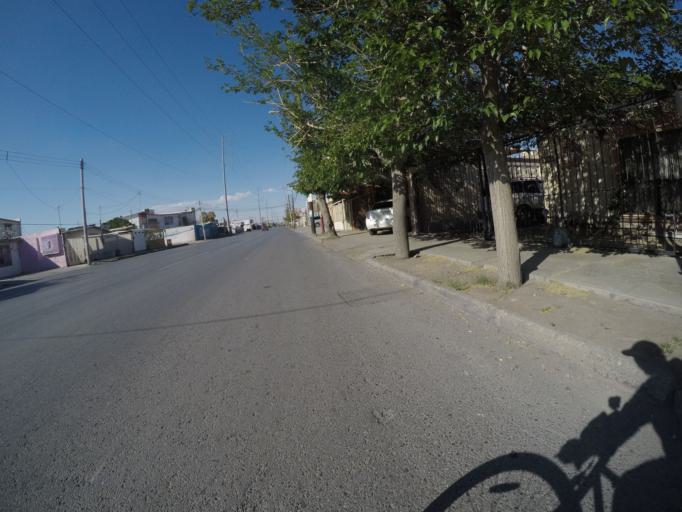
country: MX
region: Chihuahua
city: Ciudad Juarez
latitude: 31.7253
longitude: -106.4423
